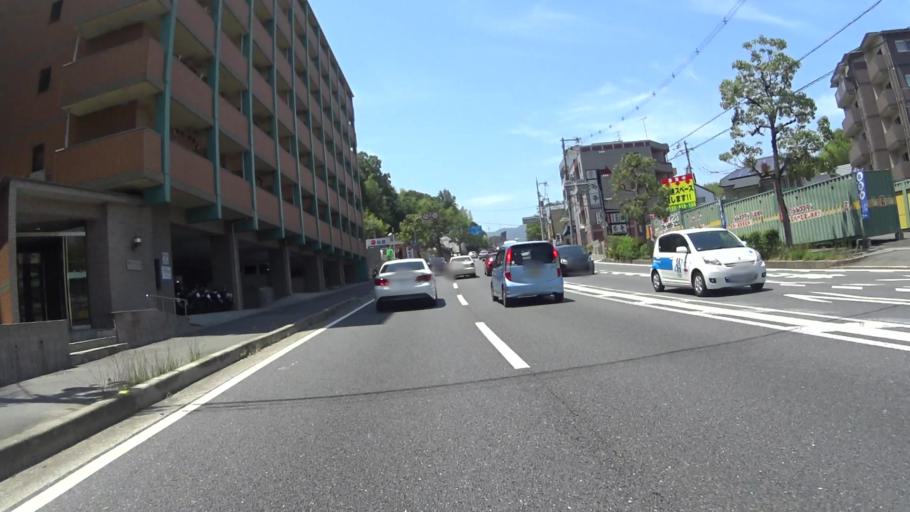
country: JP
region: Kyoto
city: Muko
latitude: 34.9736
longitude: 135.6864
